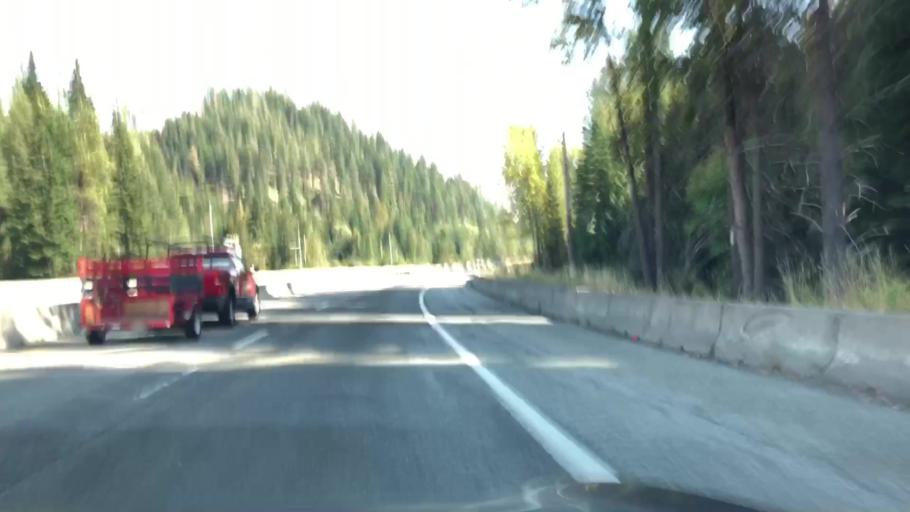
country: US
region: Idaho
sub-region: Shoshone County
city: Pinehurst
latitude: 47.5873
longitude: -116.4778
